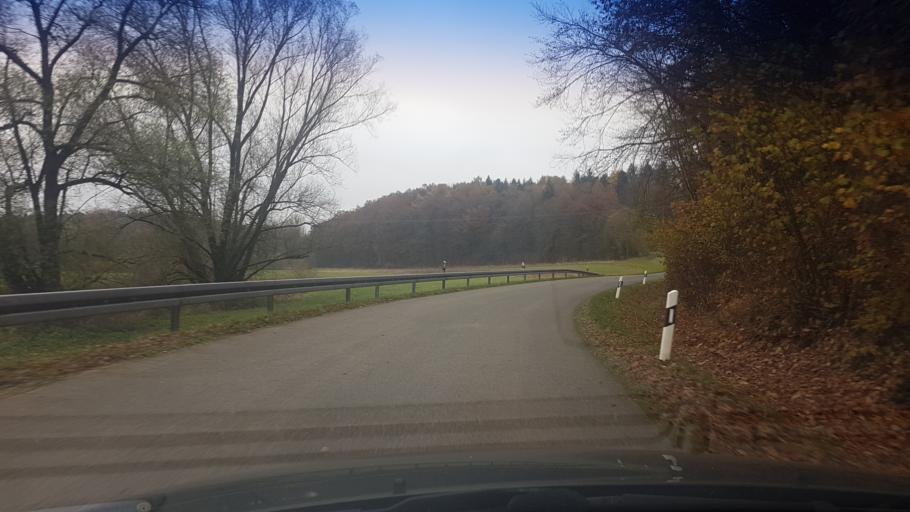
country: DE
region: Bavaria
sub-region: Upper Franconia
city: Rattelsdorf
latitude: 50.0428
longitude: 10.8747
